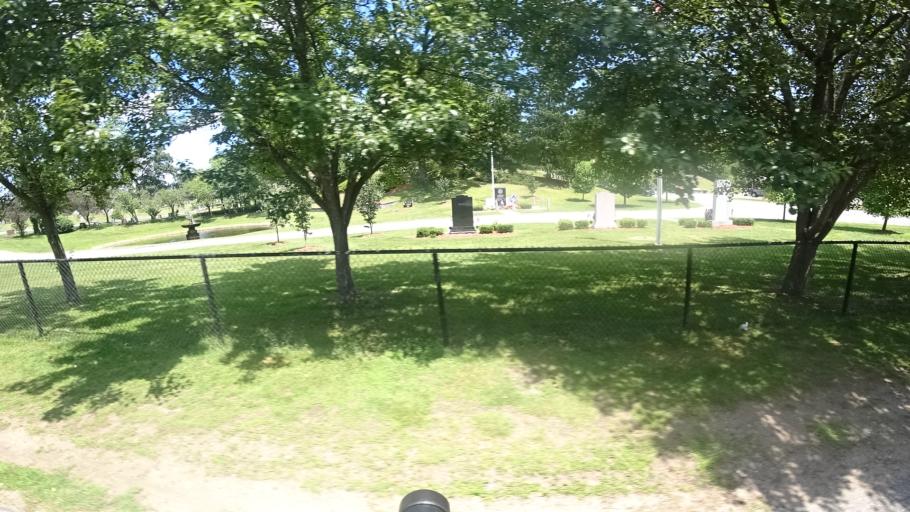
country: US
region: Massachusetts
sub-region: Norfolk County
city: Dedham
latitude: 42.2497
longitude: -71.1655
